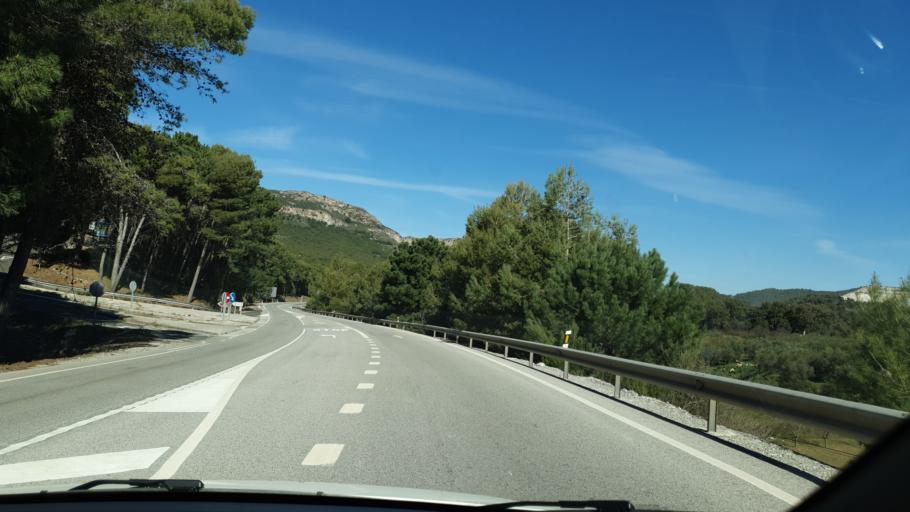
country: ES
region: Andalusia
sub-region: Provincia de Malaga
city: Ojen
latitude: 36.5910
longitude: -4.8520
